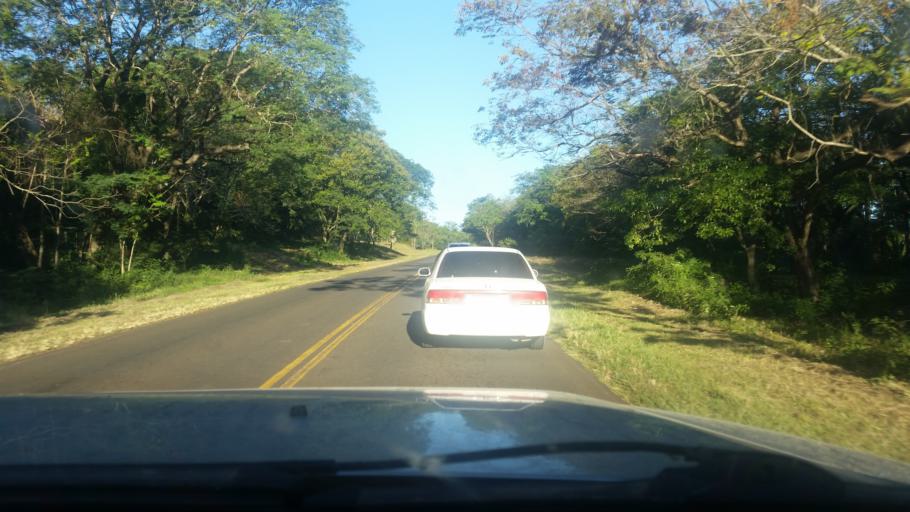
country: PY
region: Guaira
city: Independencia
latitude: -25.7154
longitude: -56.2796
